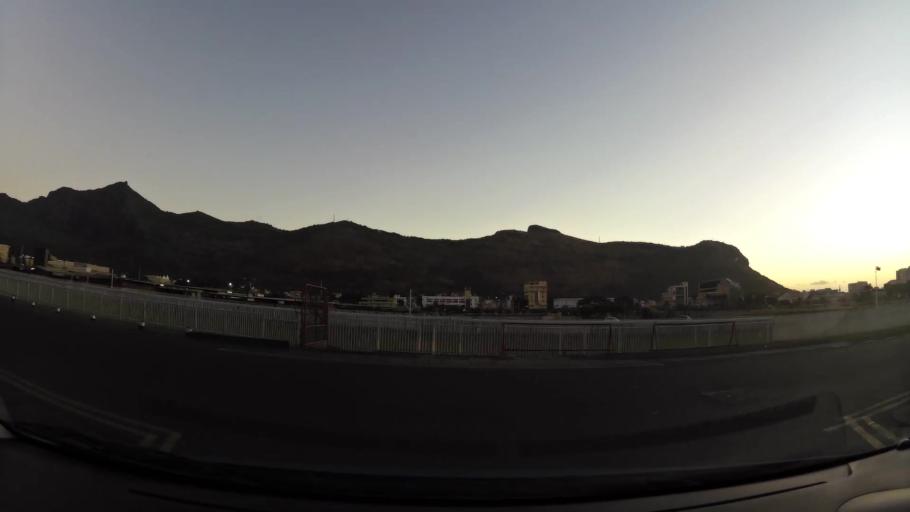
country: MU
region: Port Louis
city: Port Louis
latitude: -20.1681
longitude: 57.5118
